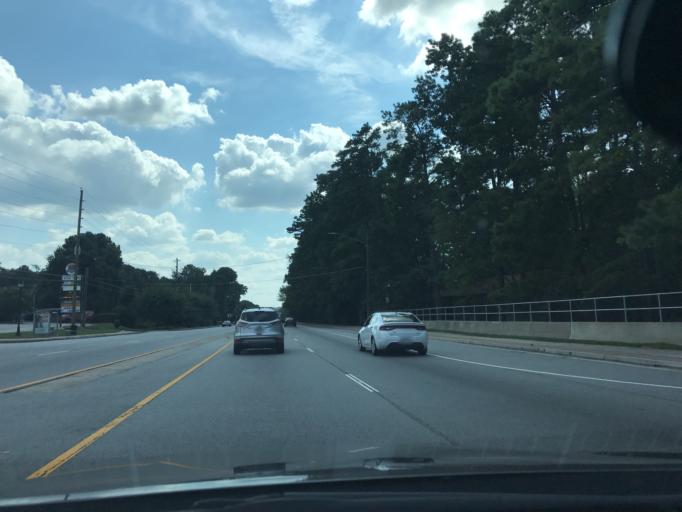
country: US
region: Georgia
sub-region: DeKalb County
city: Avondale Estates
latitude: 33.7674
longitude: -84.2526
